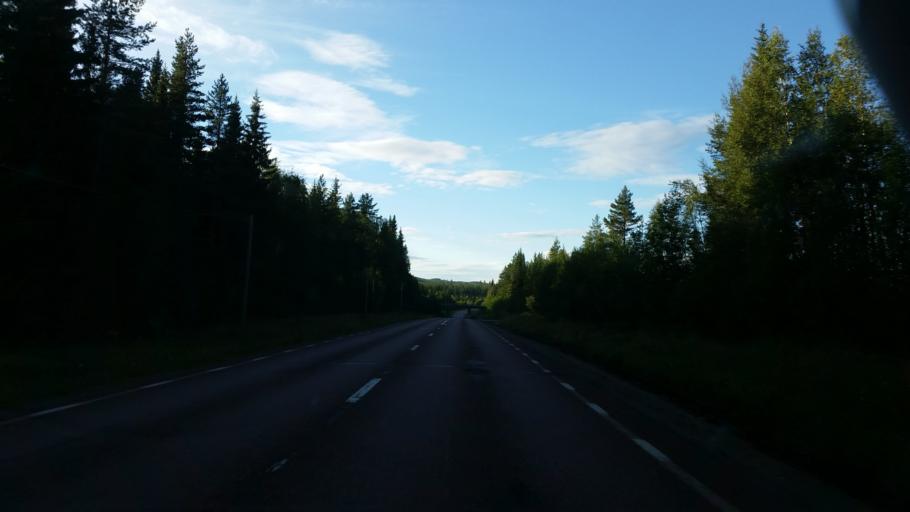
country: SE
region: Vaesterbotten
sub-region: Dorotea Kommun
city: Dorotea
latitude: 64.2036
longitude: 16.2866
